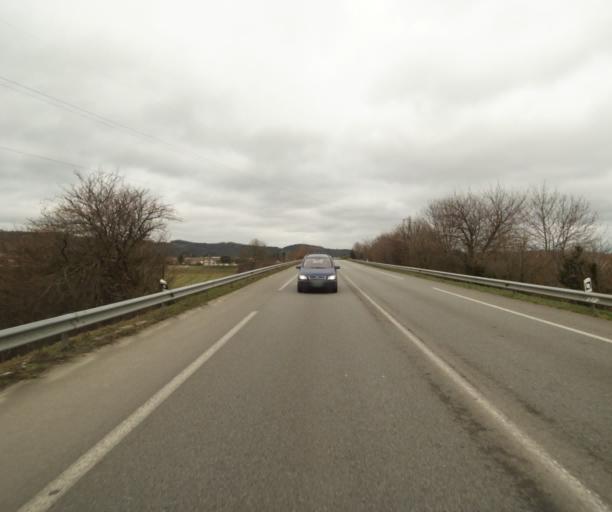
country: FR
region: Midi-Pyrenees
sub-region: Departement de l'Ariege
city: Pamiers
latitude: 43.1374
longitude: 1.6148
